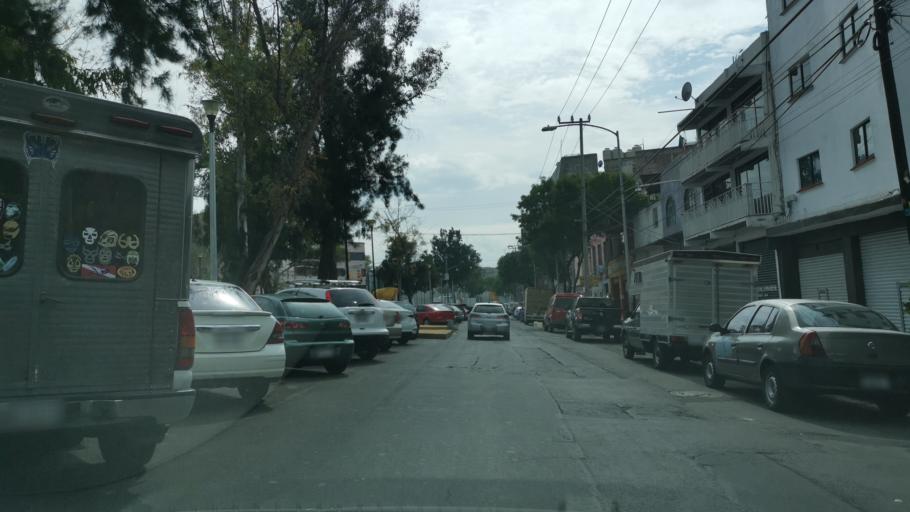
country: MX
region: Mexico City
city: Mexico City
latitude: 19.4222
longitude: -99.1281
